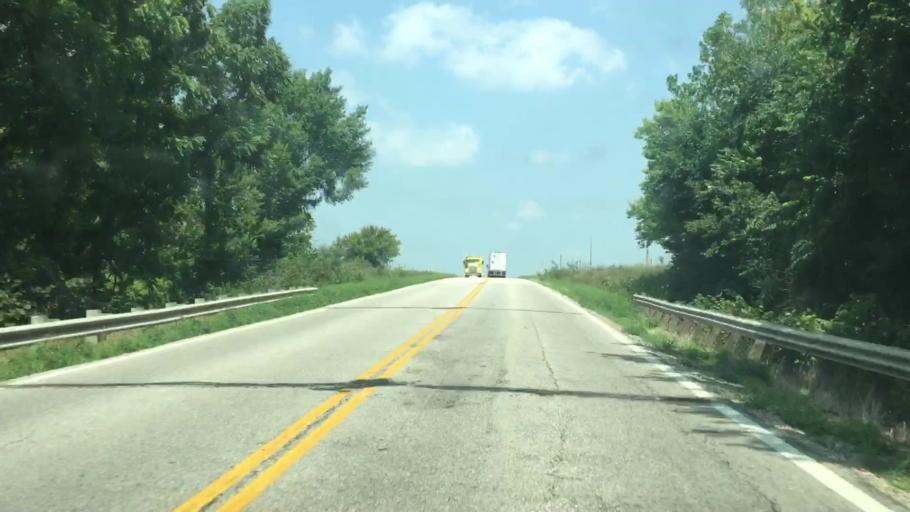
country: US
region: Kansas
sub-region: Anderson County
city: Garnett
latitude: 38.1916
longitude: -95.2535
